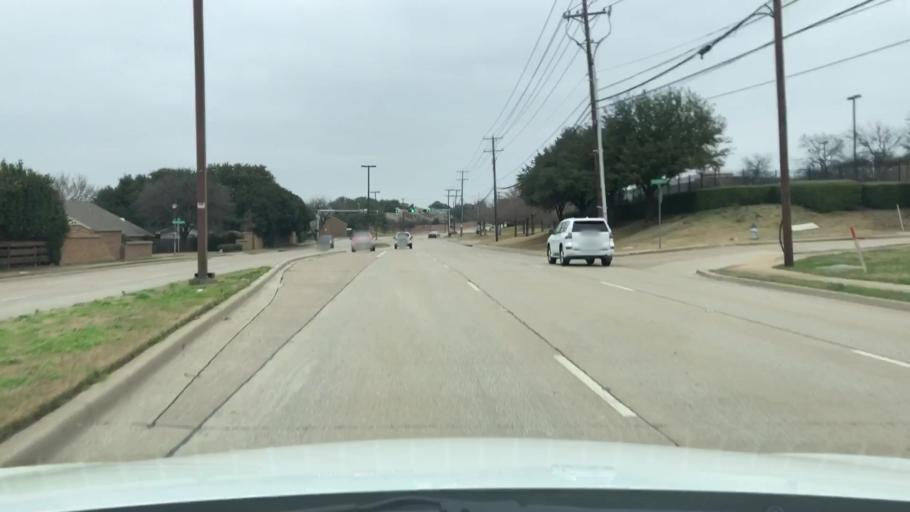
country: US
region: Texas
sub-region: Dallas County
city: Addison
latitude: 32.9791
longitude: -96.8556
